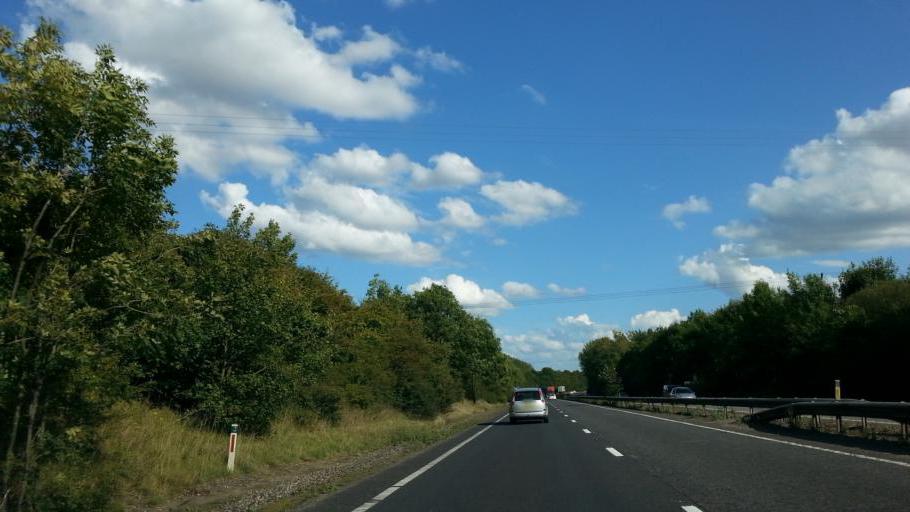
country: GB
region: England
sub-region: Suffolk
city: Needham Market
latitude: 52.1802
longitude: 1.0409
